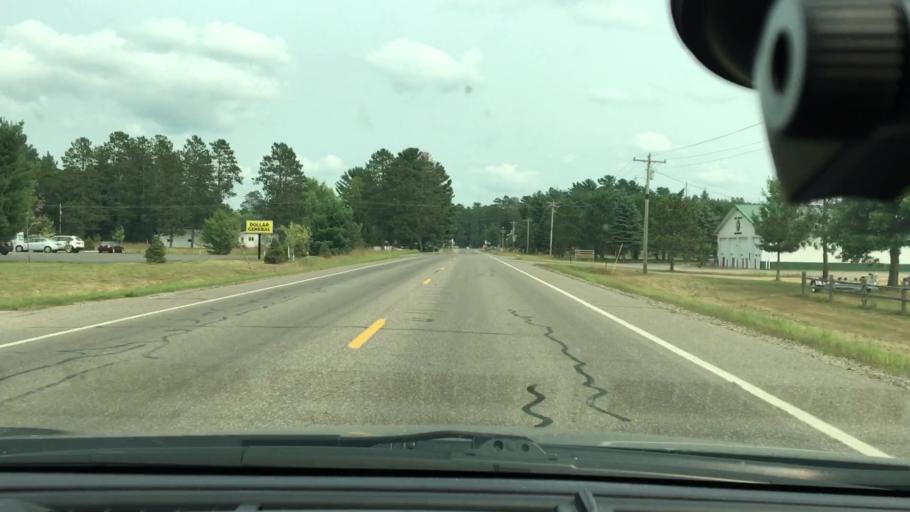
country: US
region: Minnesota
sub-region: Crow Wing County
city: Cross Lake
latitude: 46.7308
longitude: -93.9651
